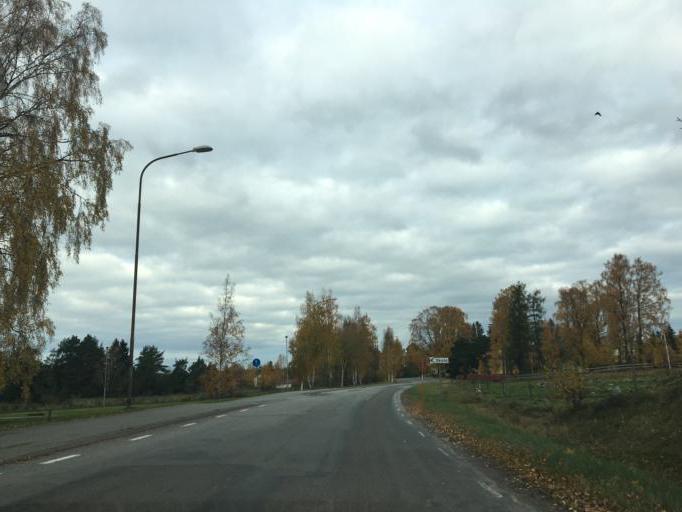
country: SE
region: Soedermanland
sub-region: Eskilstuna Kommun
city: Kvicksund
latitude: 59.5698
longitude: 16.4025
